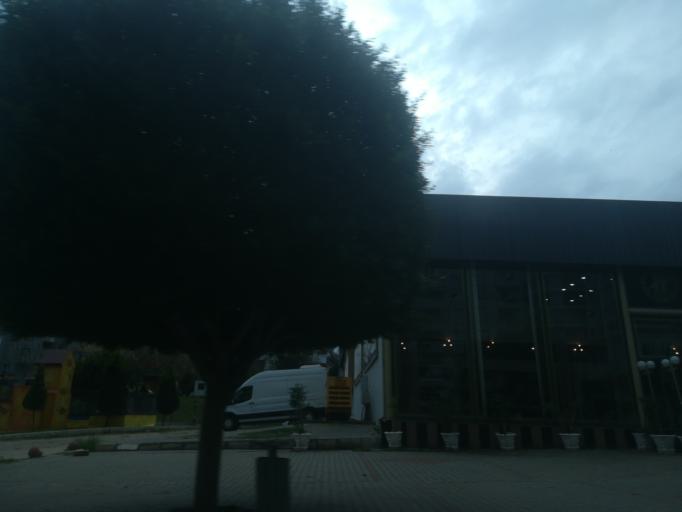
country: TR
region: Adana
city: Adana
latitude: 37.0401
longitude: 35.2926
